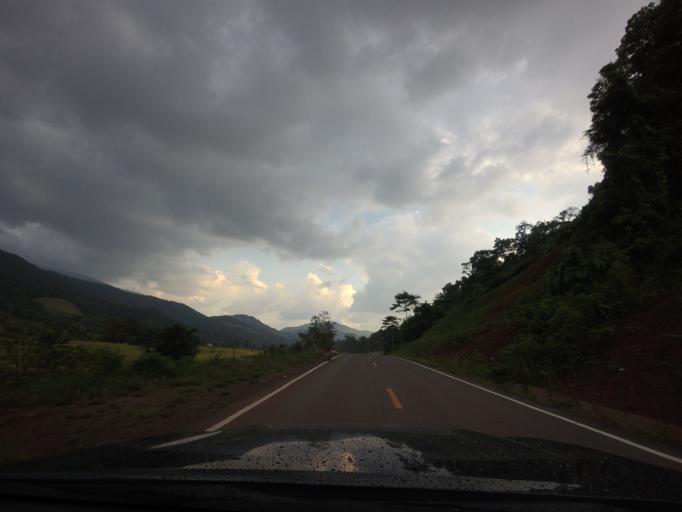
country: TH
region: Nan
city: Bo Kluea
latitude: 19.2278
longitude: 101.1825
